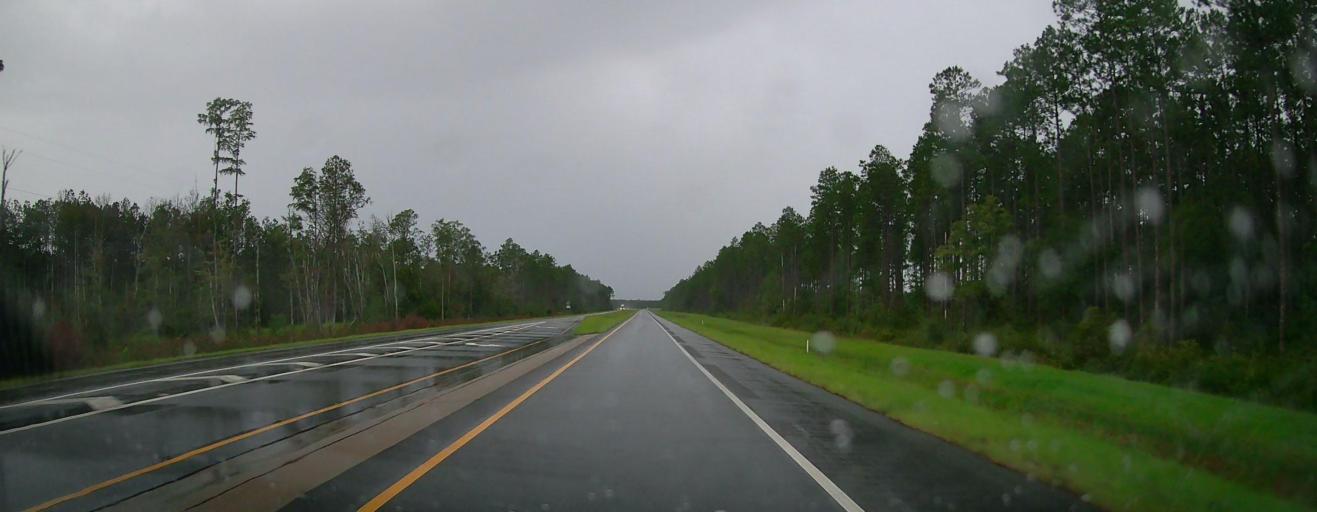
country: US
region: Georgia
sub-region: Clinch County
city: Homerville
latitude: 31.0763
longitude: -82.6514
